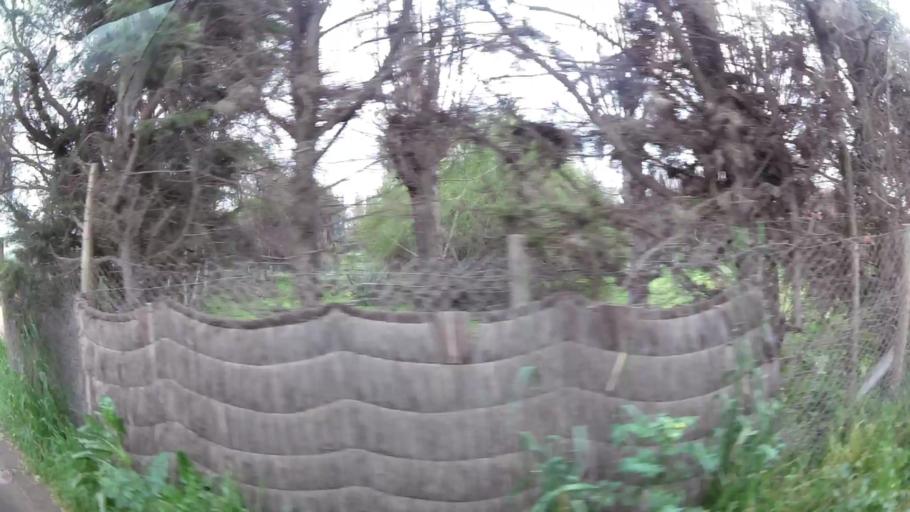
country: CL
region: Santiago Metropolitan
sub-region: Provincia de Chacabuco
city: Lampa
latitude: -33.2432
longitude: -70.7782
